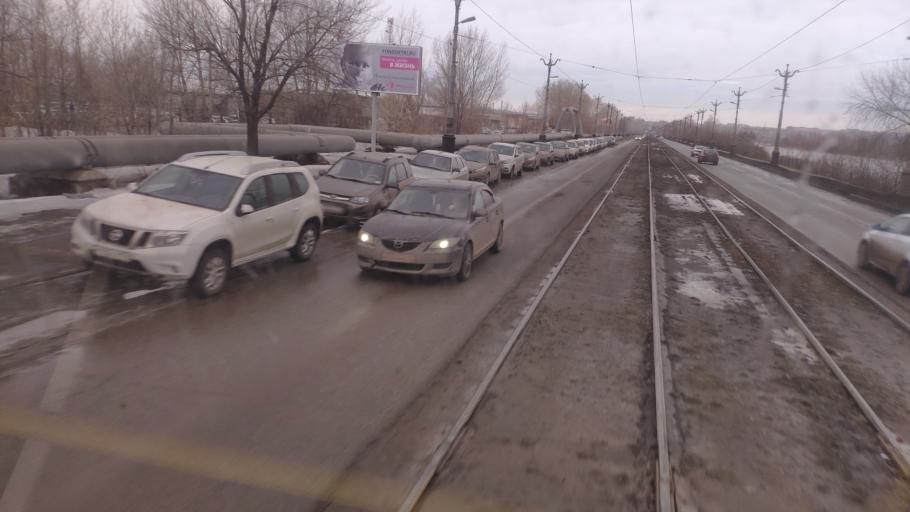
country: RU
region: Chelyabinsk
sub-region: Gorod Magnitogorsk
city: Magnitogorsk
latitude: 53.4222
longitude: 59.0279
